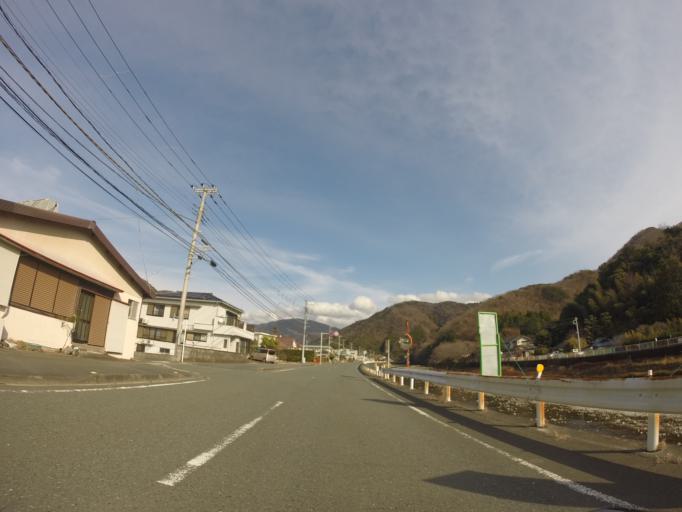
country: JP
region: Shizuoka
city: Heda
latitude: 34.7721
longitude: 138.7839
